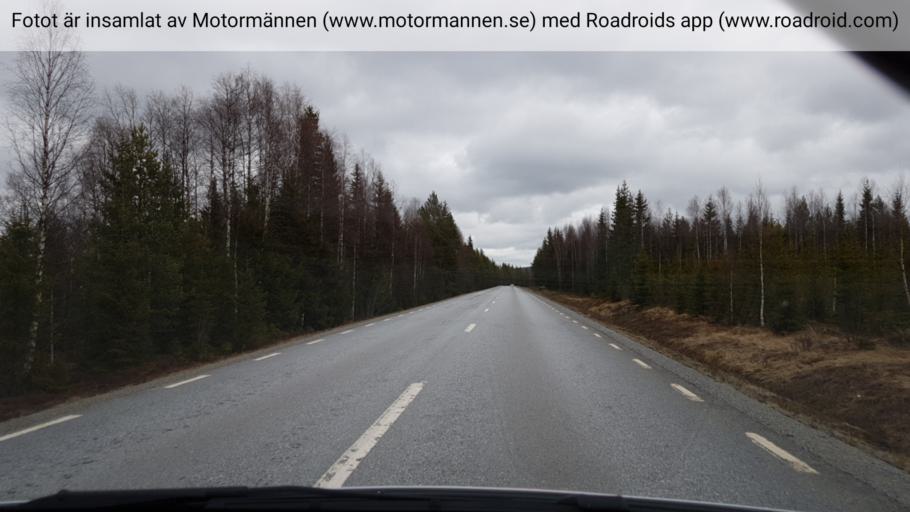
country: SE
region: Vaesterbotten
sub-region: Bjurholms Kommun
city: Bjurholm
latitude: 63.9428
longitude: 18.9213
